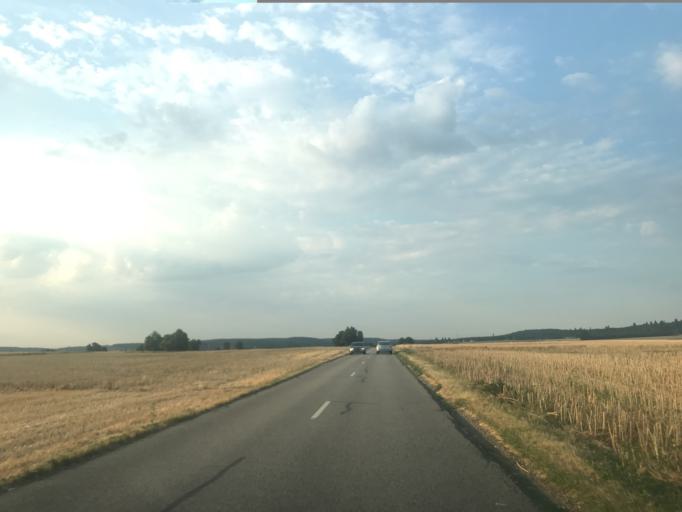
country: FR
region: Ile-de-France
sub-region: Departement des Yvelines
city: Villiers-Saint-Frederic
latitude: 48.8007
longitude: 1.8688
